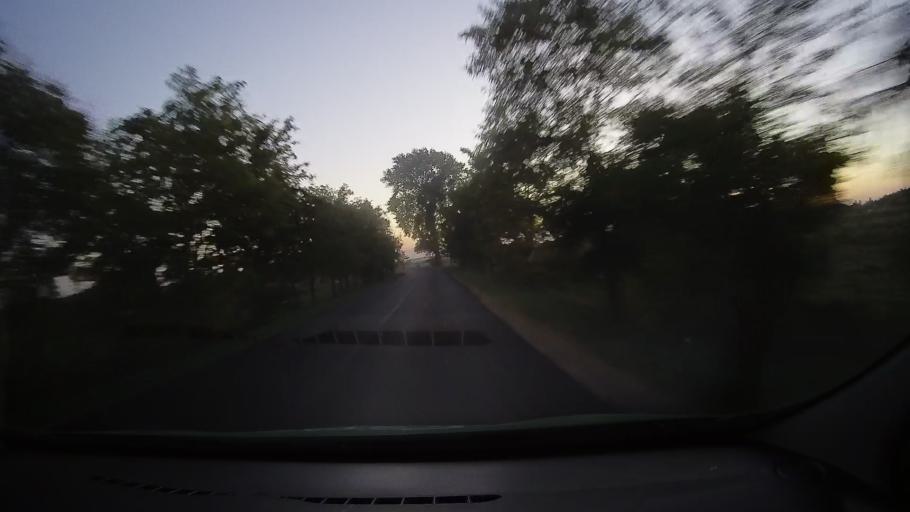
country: RO
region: Bihor
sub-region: Comuna Simian
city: Simian
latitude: 47.5083
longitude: 22.0965
